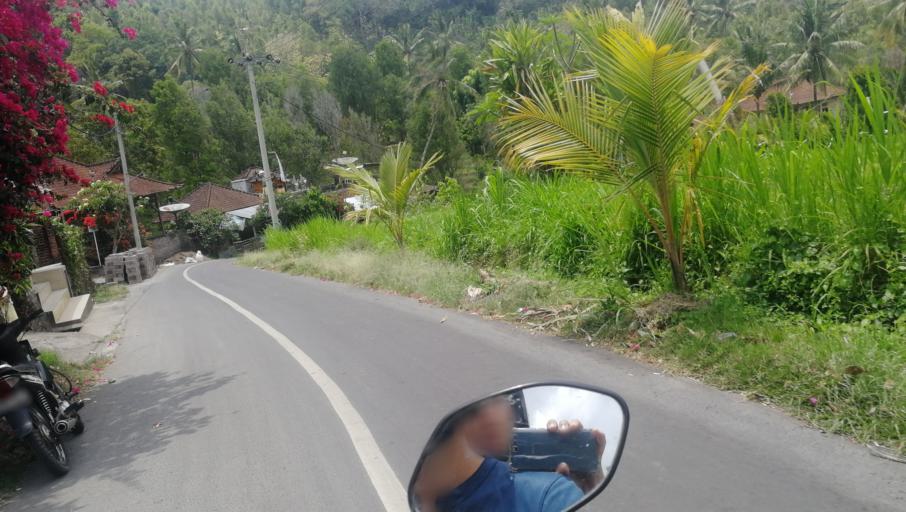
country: ID
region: Bali
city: Banjar Pedawa
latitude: -8.2653
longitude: 115.0287
